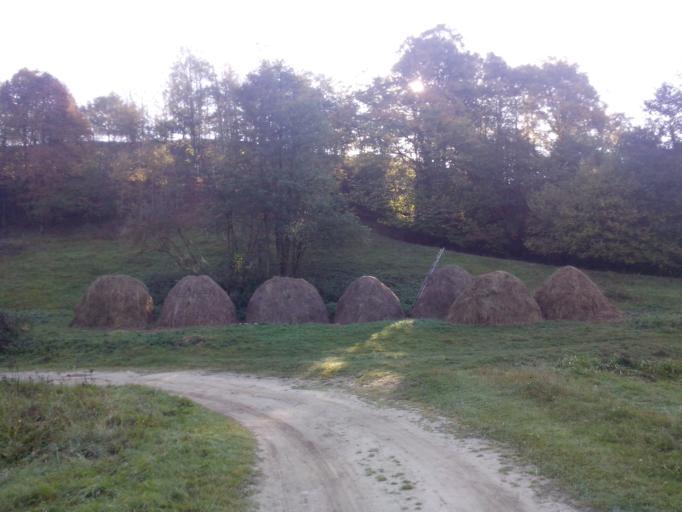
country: PL
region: Kujawsko-Pomorskie
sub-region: Powiat brodnicki
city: Gorzno
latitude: 53.2133
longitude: 19.6546
